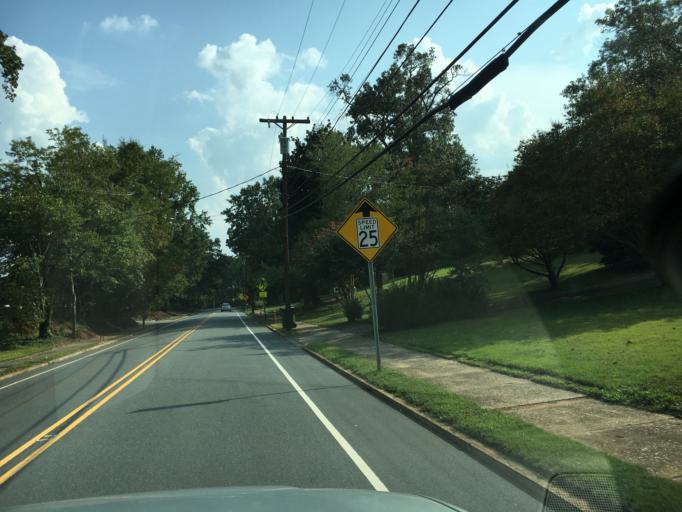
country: US
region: North Carolina
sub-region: Rutherford County
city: Rutherfordton
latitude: 35.3765
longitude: -81.9561
